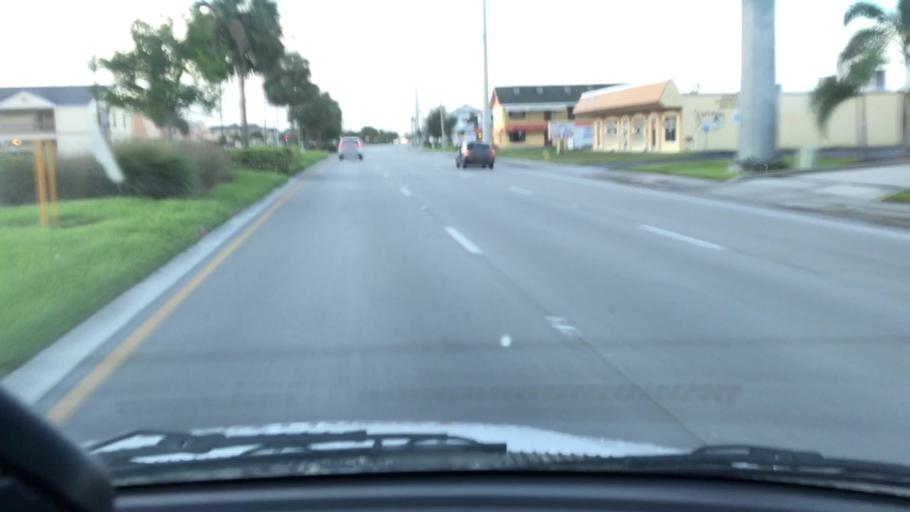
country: US
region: Florida
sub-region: Lee County
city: Cape Coral
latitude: 26.5834
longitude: -81.9421
